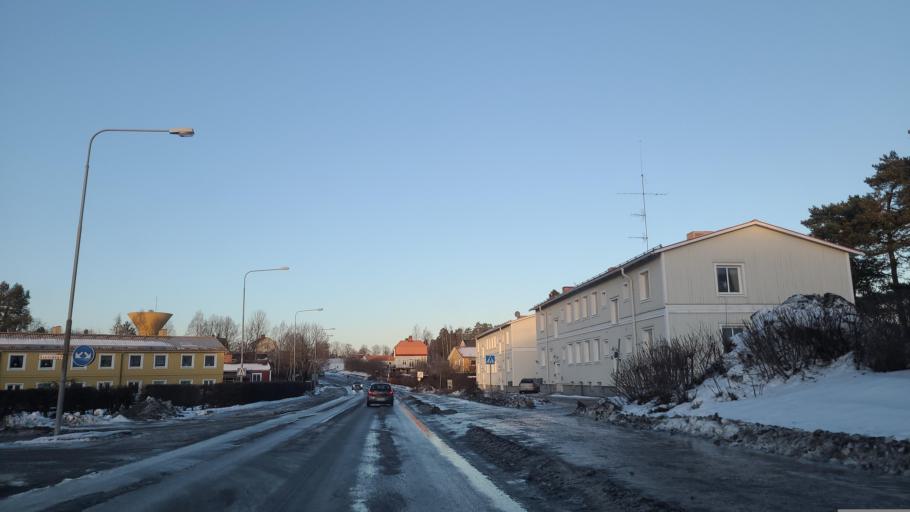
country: SE
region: Gaevleborg
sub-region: Soderhamns Kommun
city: Soderhamn
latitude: 61.3085
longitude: 17.0604
